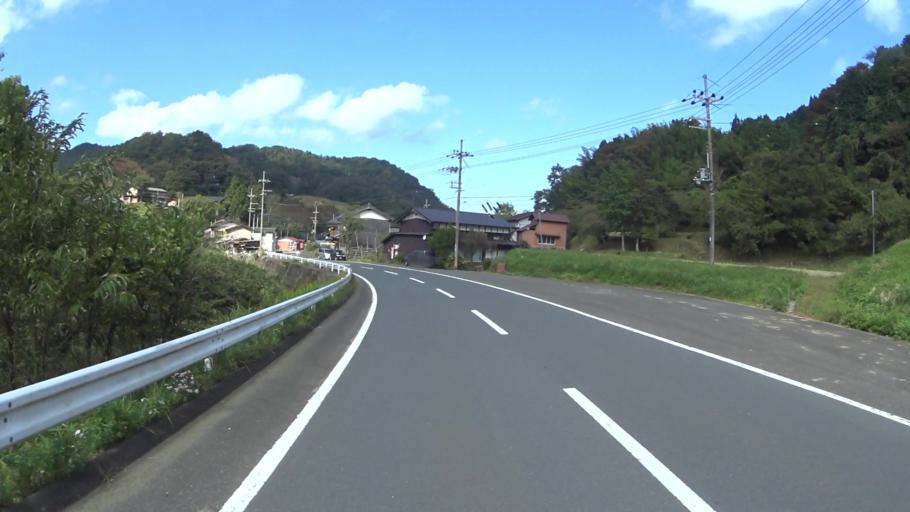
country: JP
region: Kyoto
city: Miyazu
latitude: 35.6961
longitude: 135.2513
